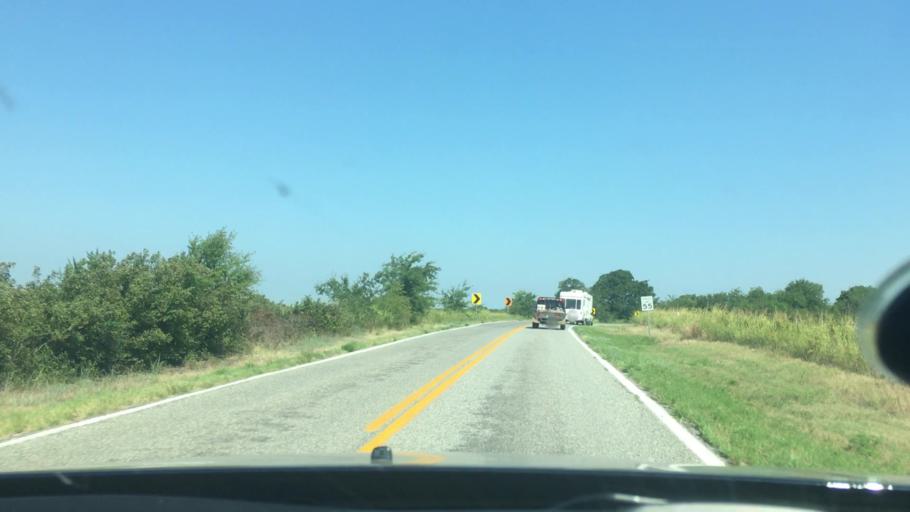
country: US
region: Oklahoma
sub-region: Johnston County
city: Tishomingo
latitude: 34.1982
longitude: -96.5414
